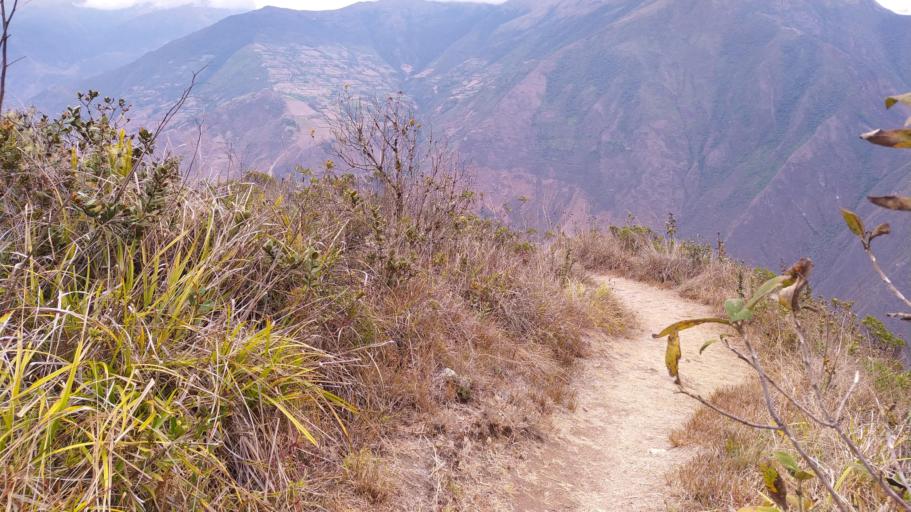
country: PE
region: Apurimac
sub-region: Provincia de Abancay
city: Huanipaca
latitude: -13.3955
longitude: -72.8742
